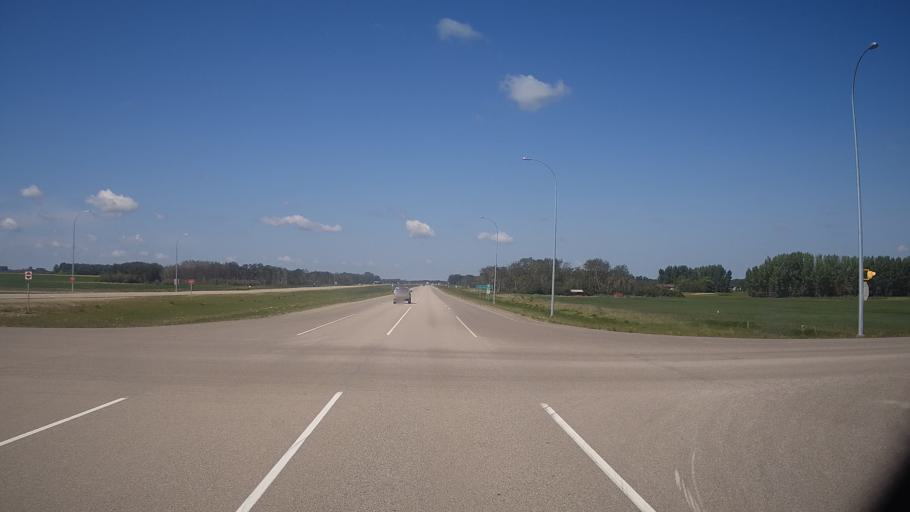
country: CA
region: Saskatchewan
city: Saskatoon
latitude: 52.0123
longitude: -106.3848
